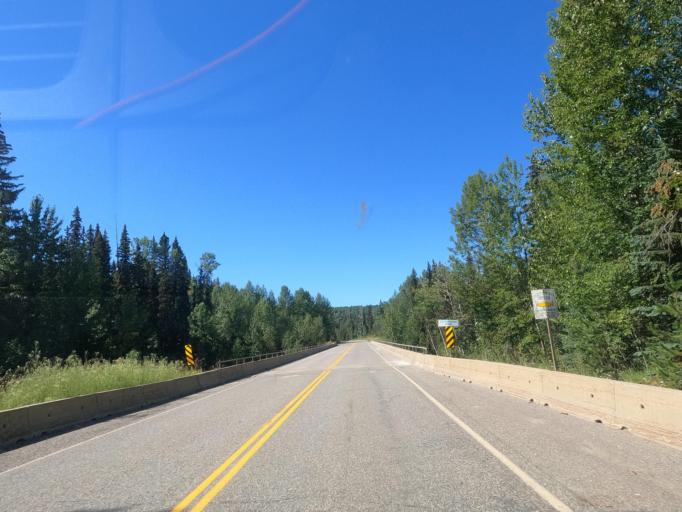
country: CA
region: British Columbia
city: Quesnel
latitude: 53.0545
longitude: -122.1760
